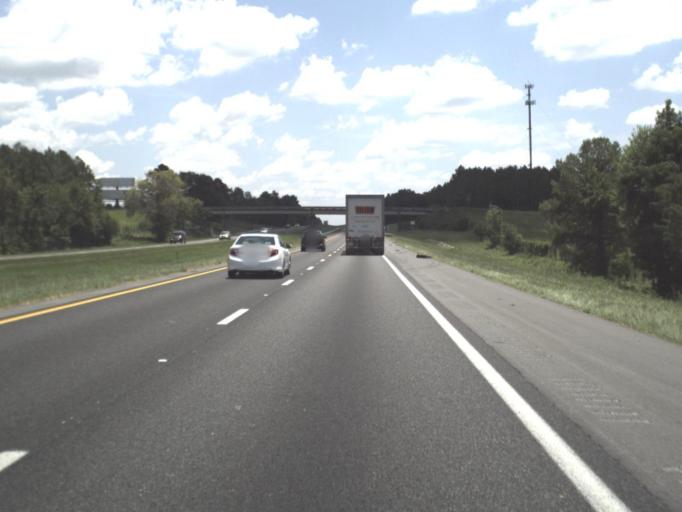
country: US
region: Florida
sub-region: Madison County
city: Madison
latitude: 30.4357
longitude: -83.5001
